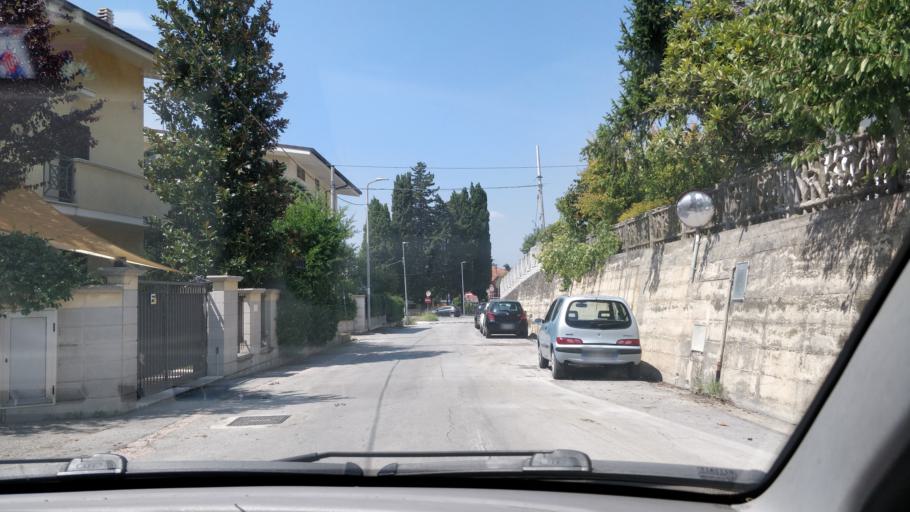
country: IT
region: Abruzzo
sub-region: Provincia di Chieti
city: Sambuceto
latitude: 42.3995
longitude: 14.1685
